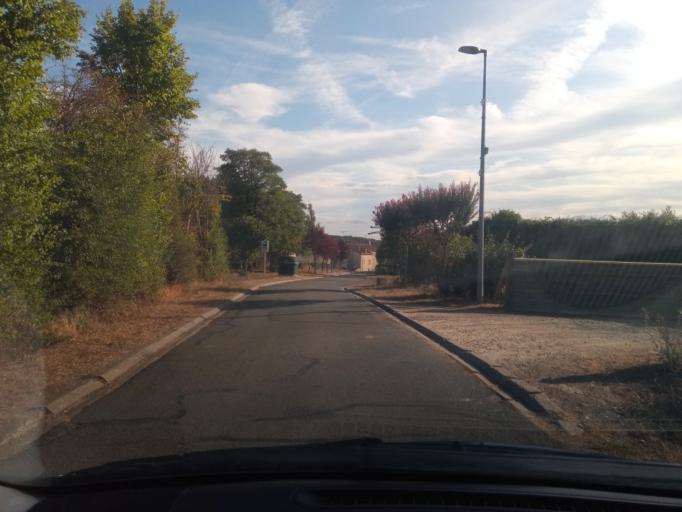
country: FR
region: Poitou-Charentes
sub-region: Departement de la Vienne
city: Montmorillon
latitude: 46.4930
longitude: 0.8127
